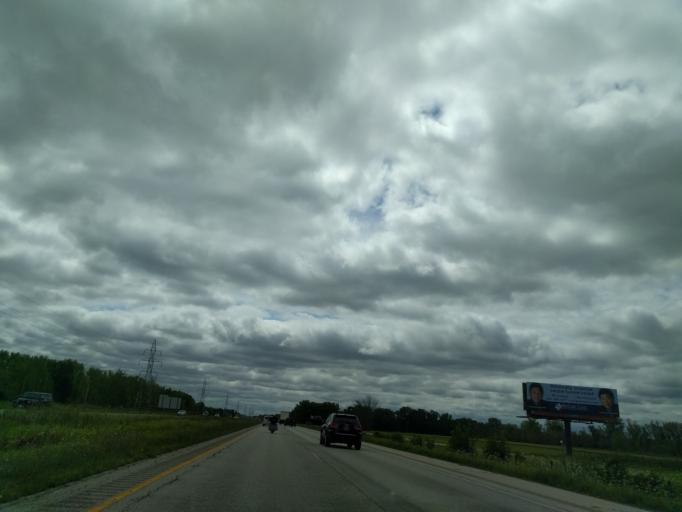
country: US
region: Wisconsin
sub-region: Brown County
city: Suamico
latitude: 44.6185
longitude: -88.0501
